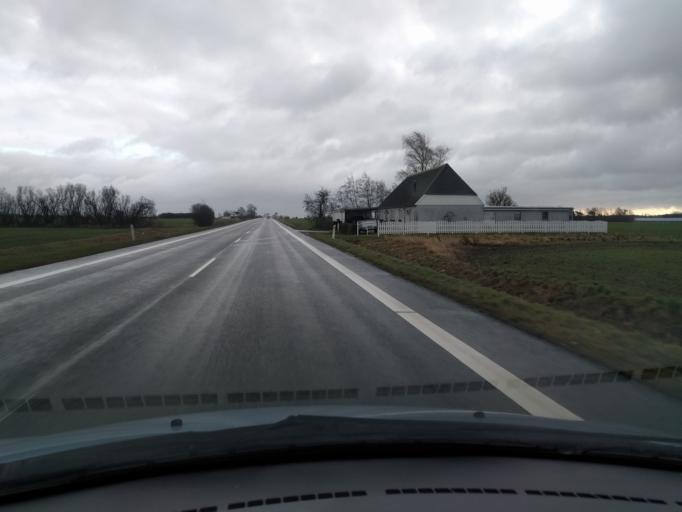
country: DK
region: South Denmark
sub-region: Kerteminde Kommune
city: Langeskov
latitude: 55.3840
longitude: 10.5323
